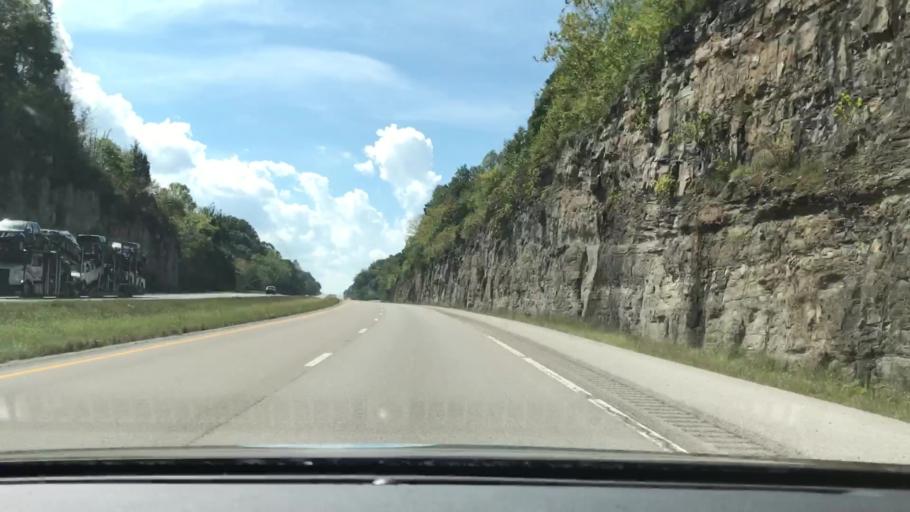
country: US
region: Kentucky
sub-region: Metcalfe County
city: Edmonton
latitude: 37.0252
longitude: -85.5529
